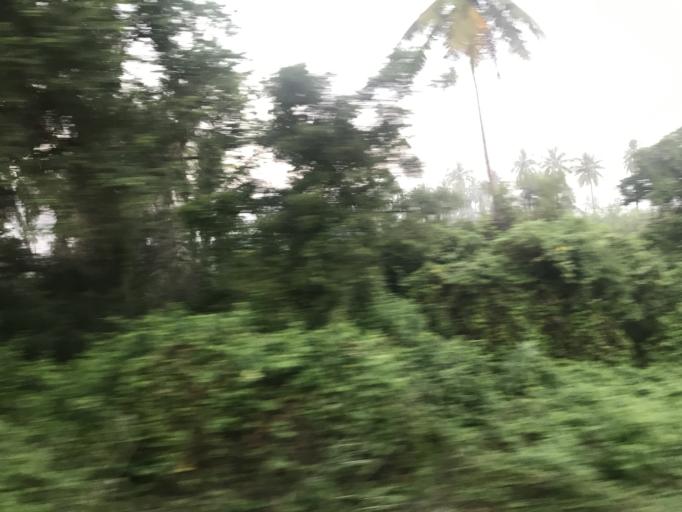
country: IN
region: Andhra Pradesh
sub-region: Guntur
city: Ponnur
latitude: 16.0775
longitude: 80.5618
